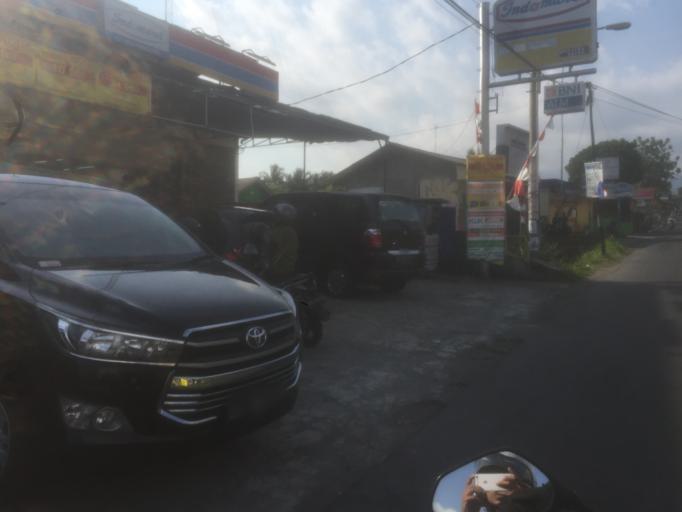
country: ID
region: Daerah Istimewa Yogyakarta
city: Sleman
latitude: -7.6707
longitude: 110.4175
